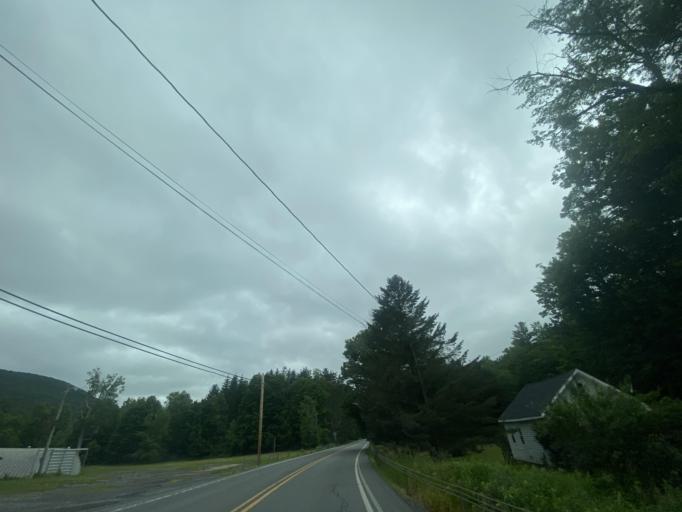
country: US
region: New York
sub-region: Schoharie County
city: Middleburgh
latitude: 42.3839
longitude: -74.3814
